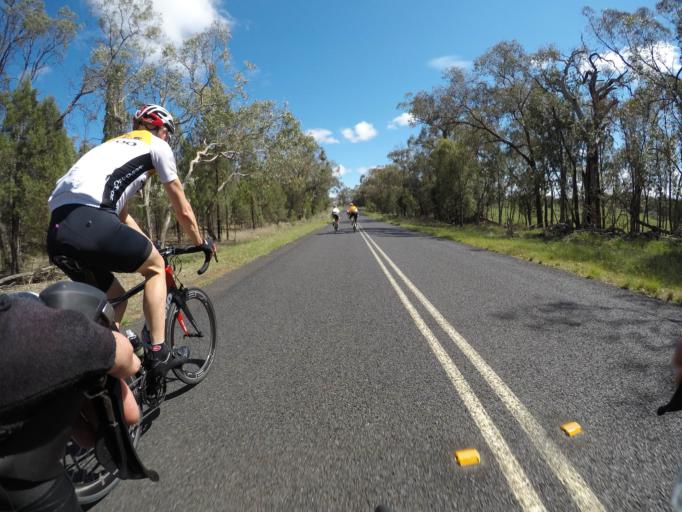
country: AU
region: New South Wales
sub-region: Dubbo Municipality
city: Eulomogo
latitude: -32.5996
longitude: 148.5440
